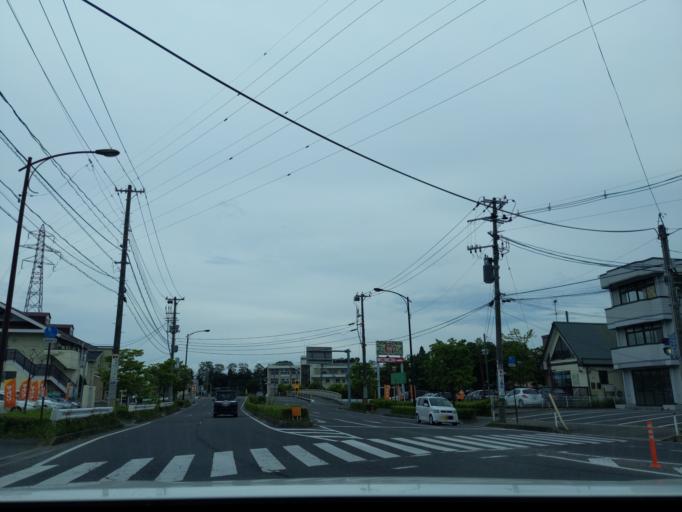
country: JP
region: Fukushima
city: Koriyama
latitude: 37.3674
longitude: 140.3626
